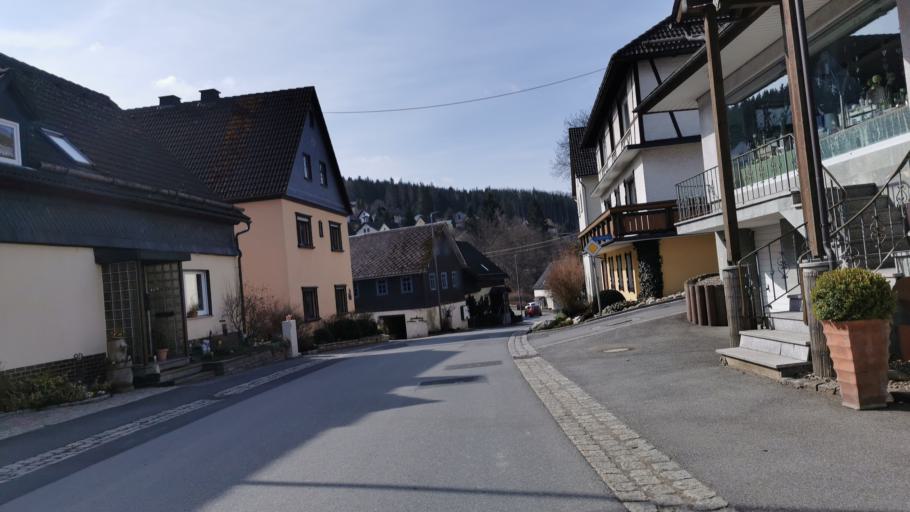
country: DE
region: Bavaria
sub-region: Upper Franconia
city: Teuschnitz
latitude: 50.4271
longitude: 11.3373
